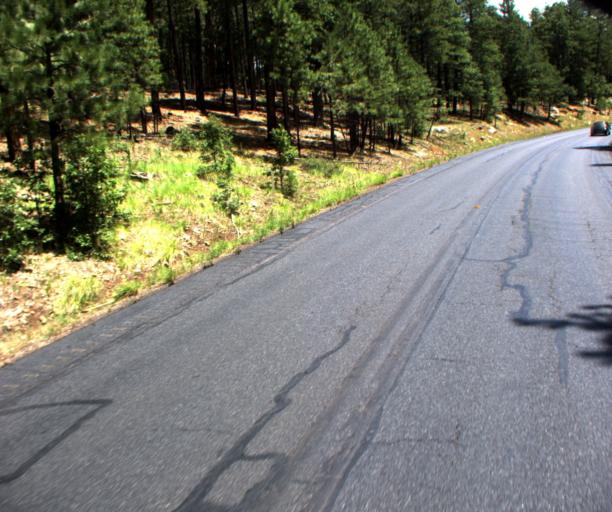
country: US
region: Arizona
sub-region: Gila County
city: Pine
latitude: 34.4596
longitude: -111.4396
